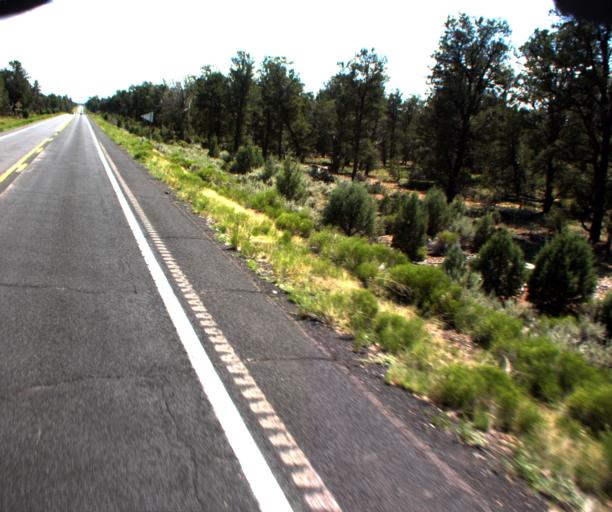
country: US
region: Arizona
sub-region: Coconino County
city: Grand Canyon Village
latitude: 35.8785
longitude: -112.1323
